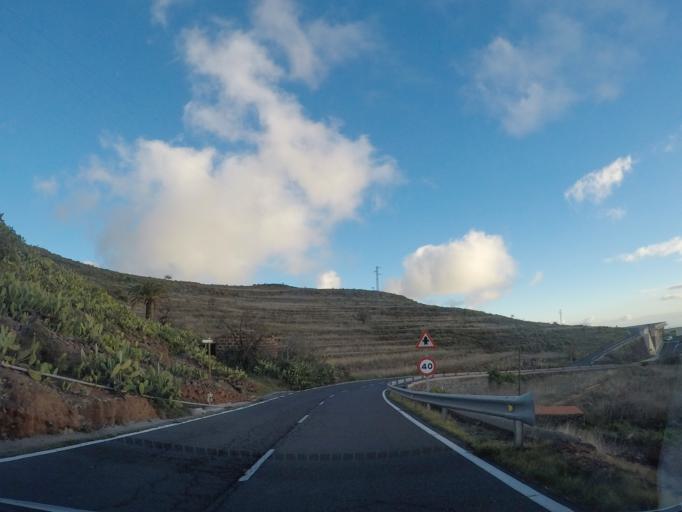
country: ES
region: Canary Islands
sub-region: Provincia de Santa Cruz de Tenerife
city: Alajero
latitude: 28.0718
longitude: -17.2378
